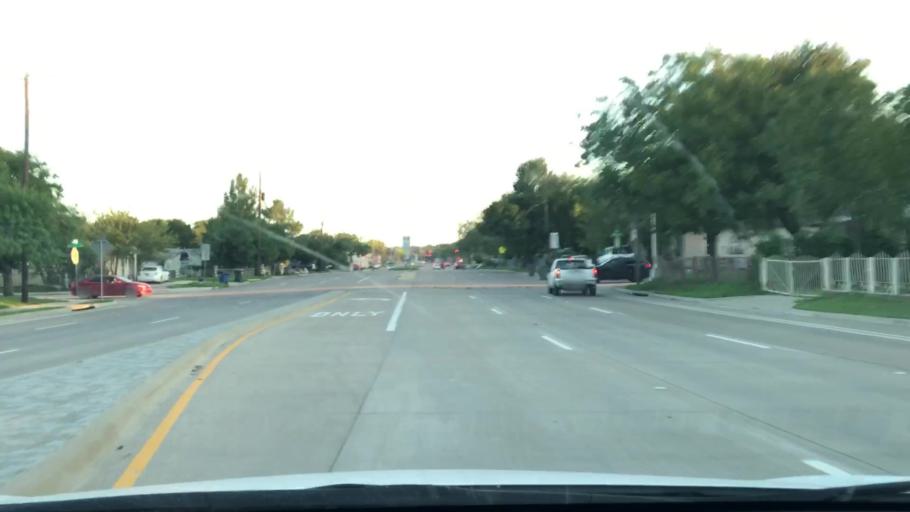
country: US
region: Texas
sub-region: Dallas County
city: Dallas
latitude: 32.7843
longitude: -96.8358
